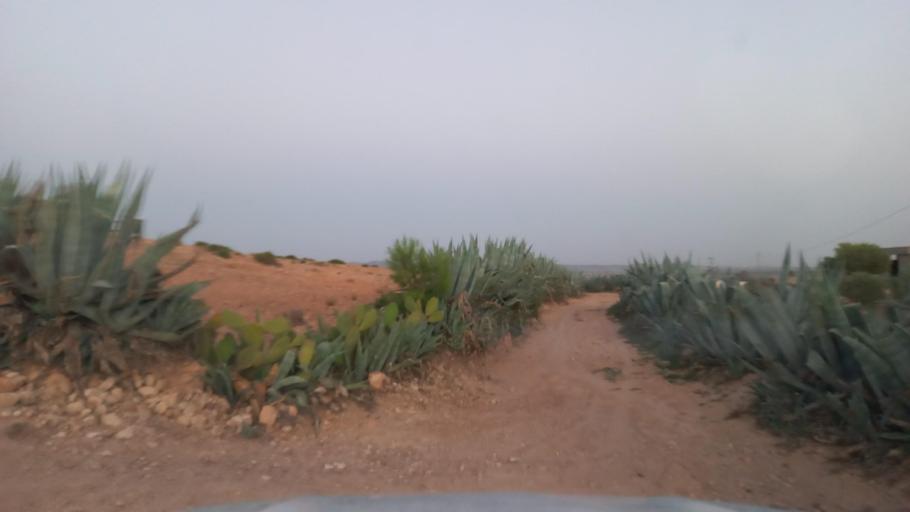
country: TN
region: Al Qasrayn
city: Sbiba
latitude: 35.3778
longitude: 9.0115
